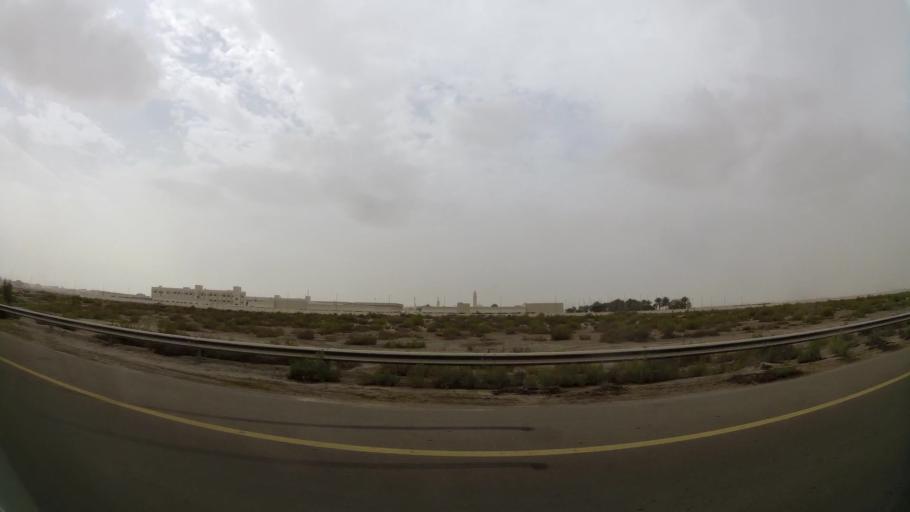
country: AE
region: Abu Dhabi
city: Abu Dhabi
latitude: 24.3802
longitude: 54.6878
